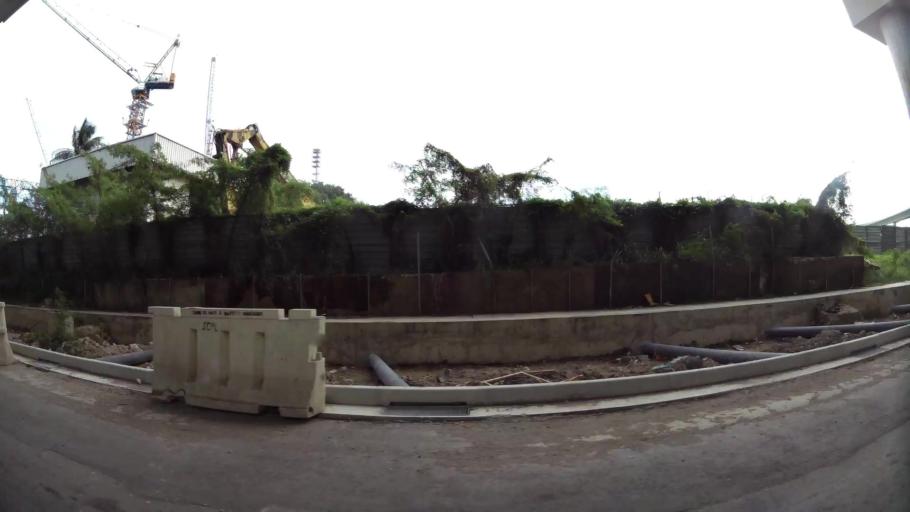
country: MY
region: Johor
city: Johor Bahru
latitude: 1.3165
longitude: 103.6540
